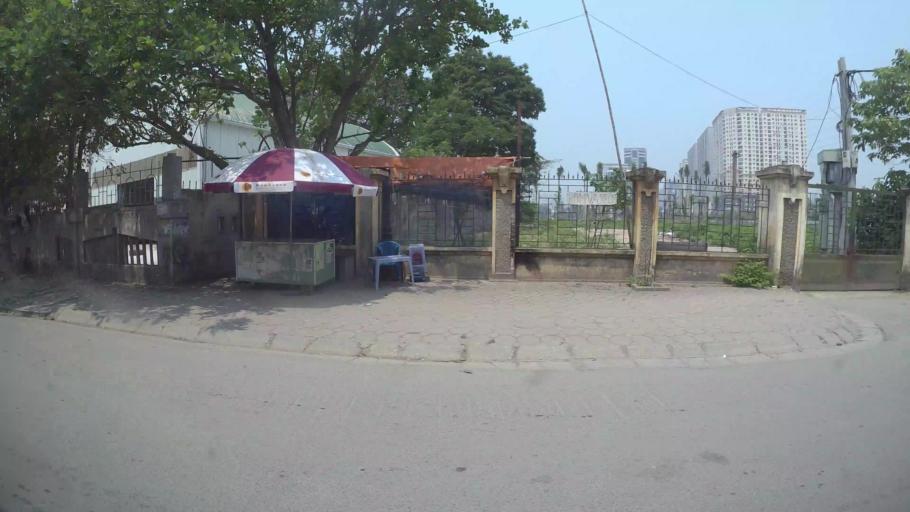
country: VN
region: Ha Noi
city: Thanh Xuan
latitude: 20.9950
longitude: 105.7897
